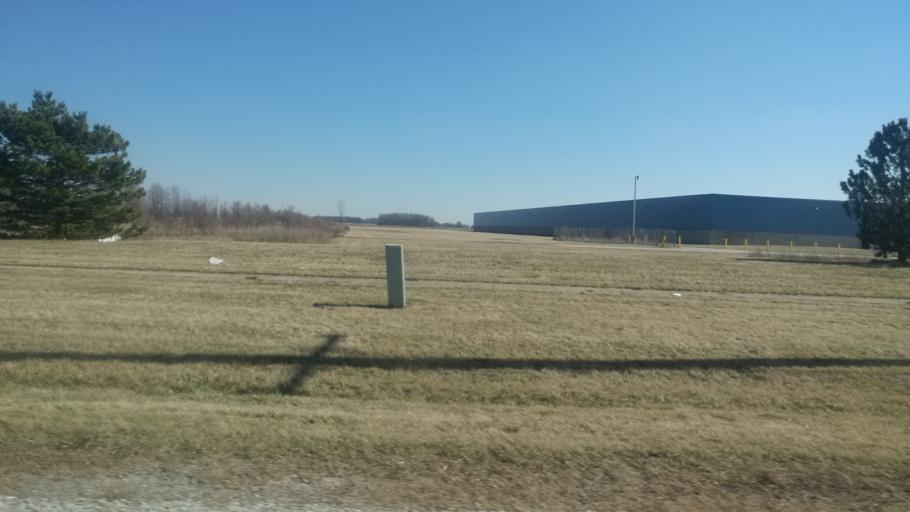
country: US
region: Ohio
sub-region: Wood County
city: Perrysburg
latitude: 41.5170
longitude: -83.6390
